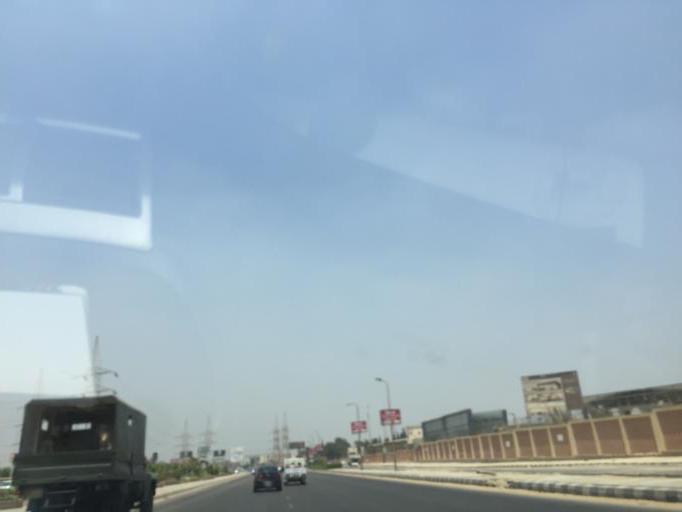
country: EG
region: Muhafazat al Qalyubiyah
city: Al Khankah
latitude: 30.0808
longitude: 31.4160
